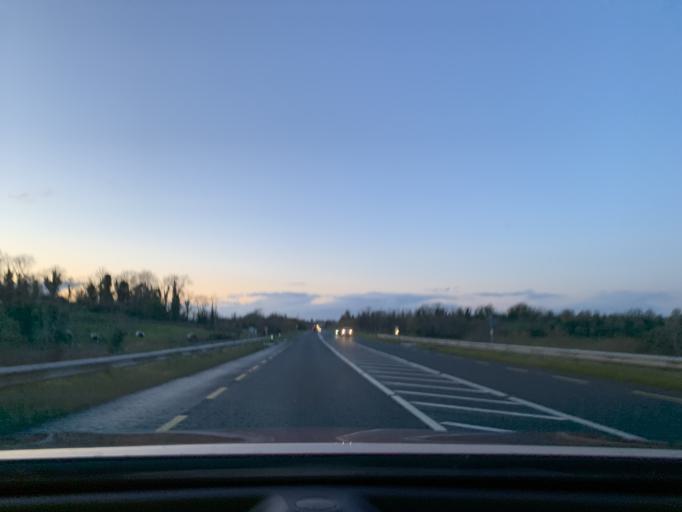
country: IE
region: Connaught
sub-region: County Leitrim
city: Carrick-on-Shannon
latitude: 53.9371
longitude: -8.0568
